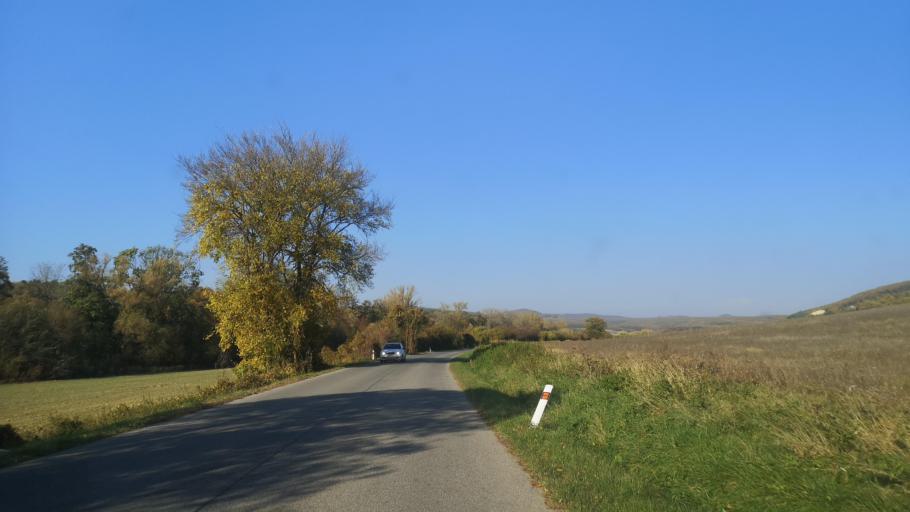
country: SK
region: Nitriansky
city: Zlate Moravce
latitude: 48.4363
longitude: 18.4302
